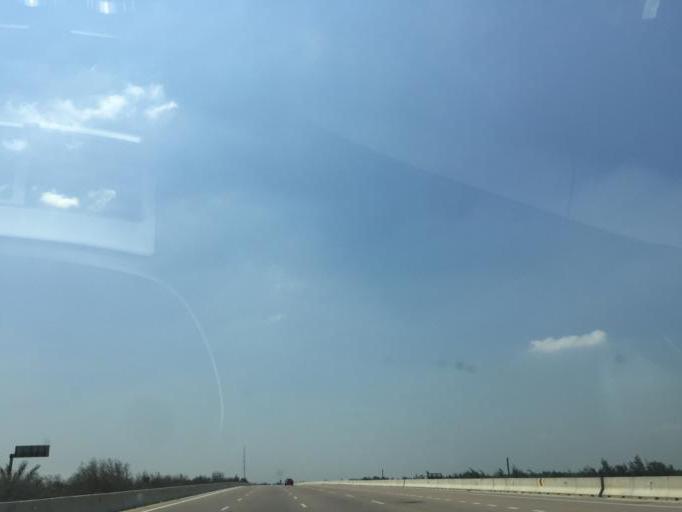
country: EG
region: Al Buhayrah
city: Beheira
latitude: 30.5367
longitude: 30.2190
